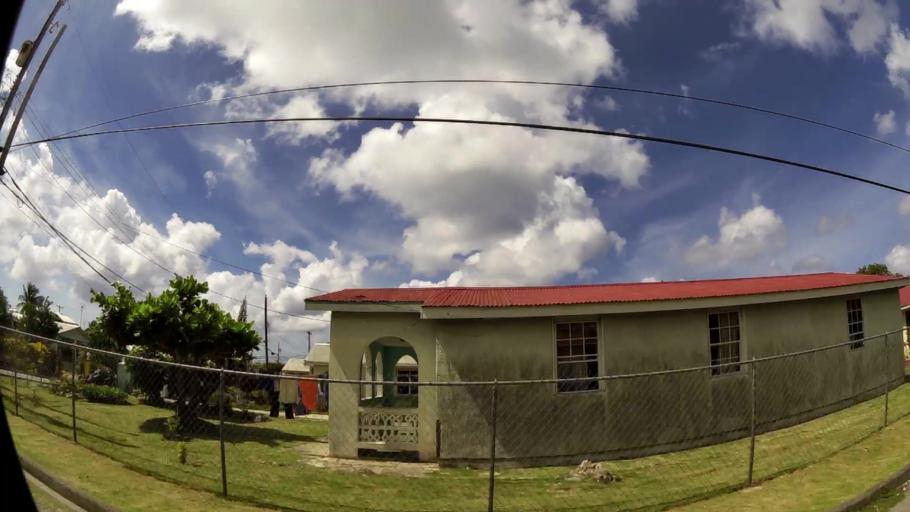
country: BB
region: Saint James
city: Holetown
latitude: 13.1497
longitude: -59.6293
